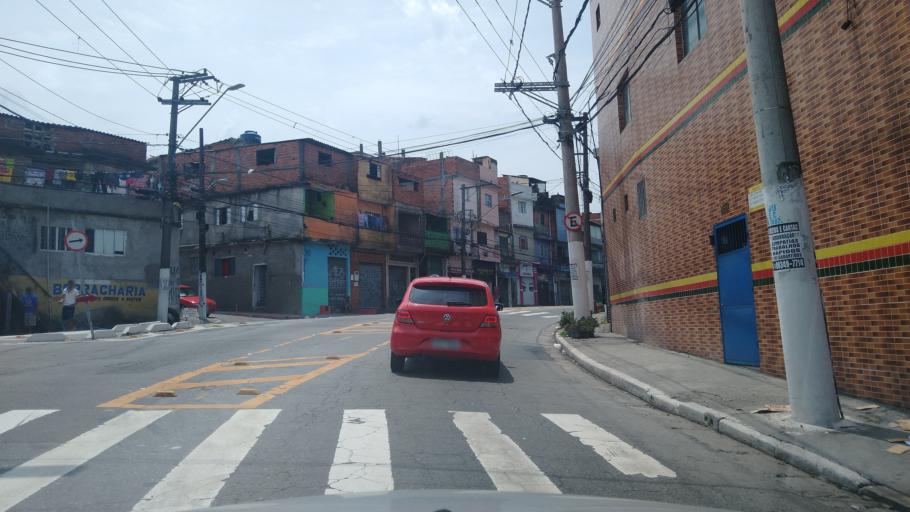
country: BR
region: Sao Paulo
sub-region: Sao Paulo
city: Sao Paulo
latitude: -23.4592
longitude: -46.6874
